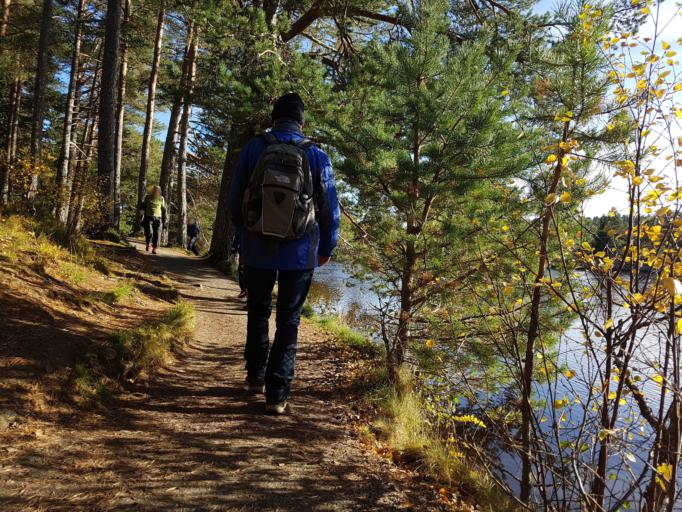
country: NO
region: Sor-Trondelag
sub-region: Trondheim
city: Trondheim
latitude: 63.4196
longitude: 10.3238
